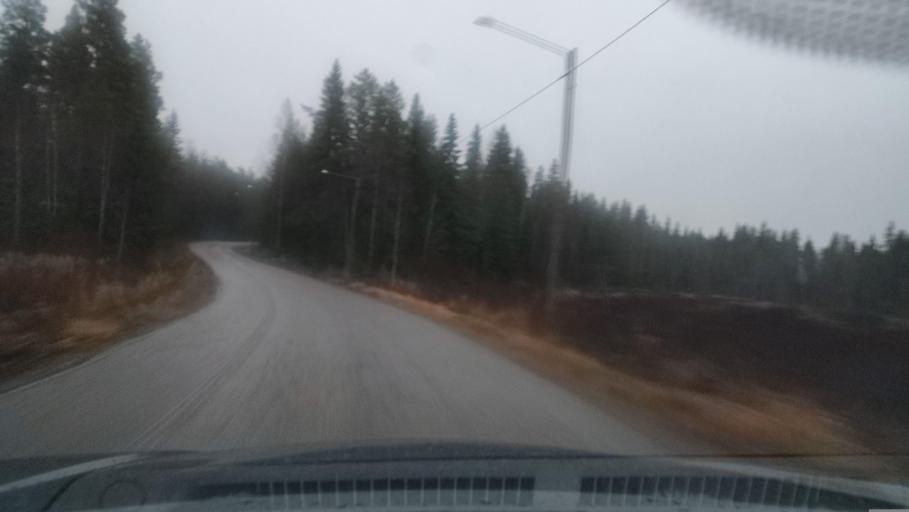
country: FI
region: Southern Ostrobothnia
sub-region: Suupohja
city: Karijoki
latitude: 62.1352
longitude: 21.5737
